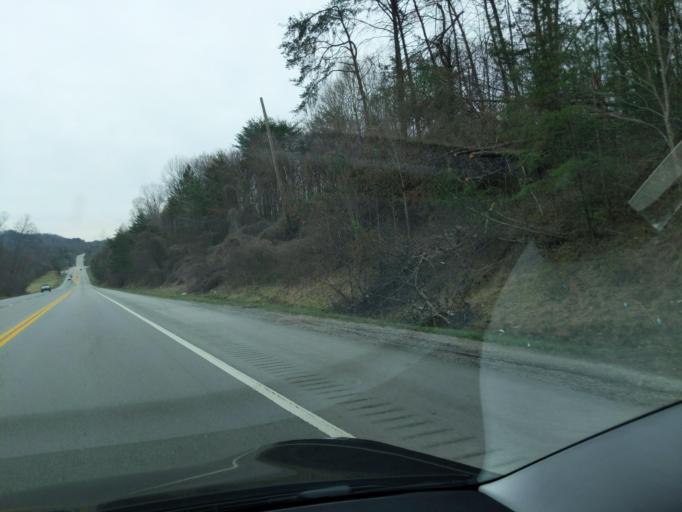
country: US
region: Kentucky
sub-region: Whitley County
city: Corbin
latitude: 36.9173
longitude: -84.0974
